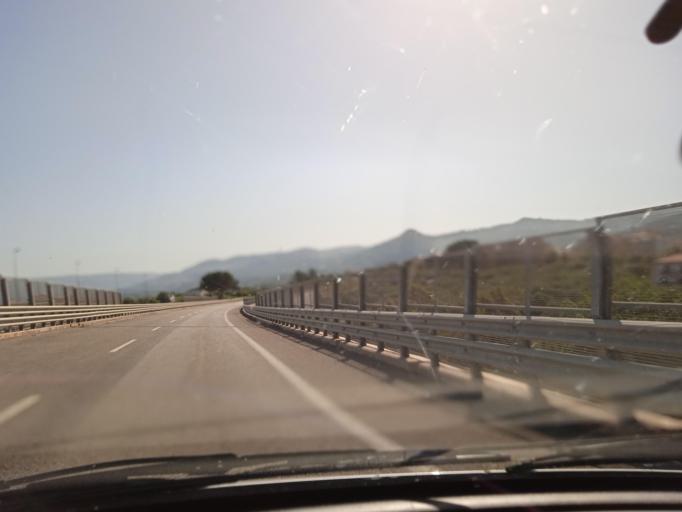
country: IT
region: Sicily
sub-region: Messina
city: Sant'Agata di Militello
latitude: 38.0598
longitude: 14.6246
